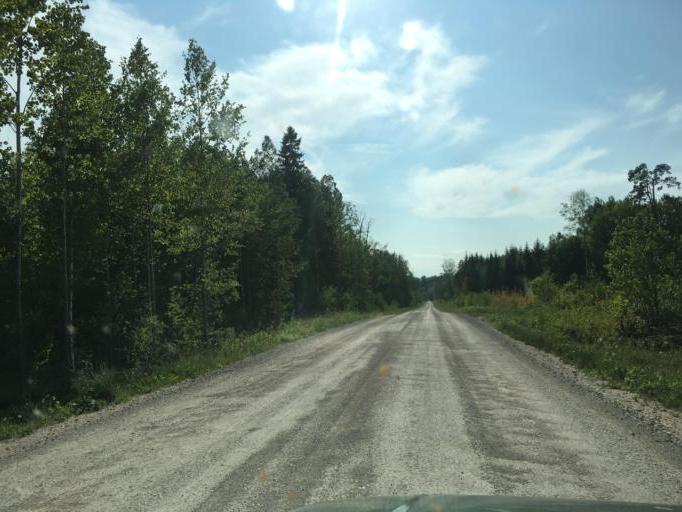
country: LV
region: Dundaga
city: Dundaga
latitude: 57.6131
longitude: 22.4964
